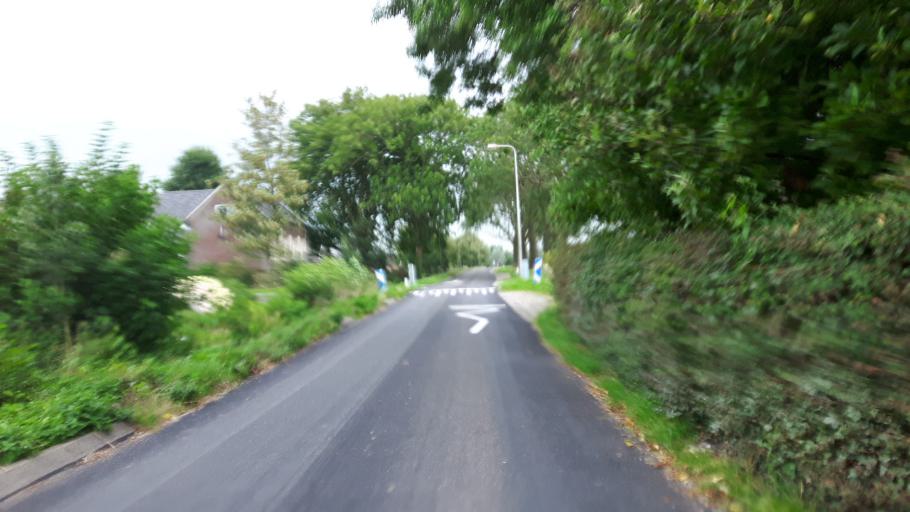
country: NL
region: South Holland
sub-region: Gemeente Alphen aan den Rijn
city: Alphen aan den Rijn
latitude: 52.1149
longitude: 4.7031
